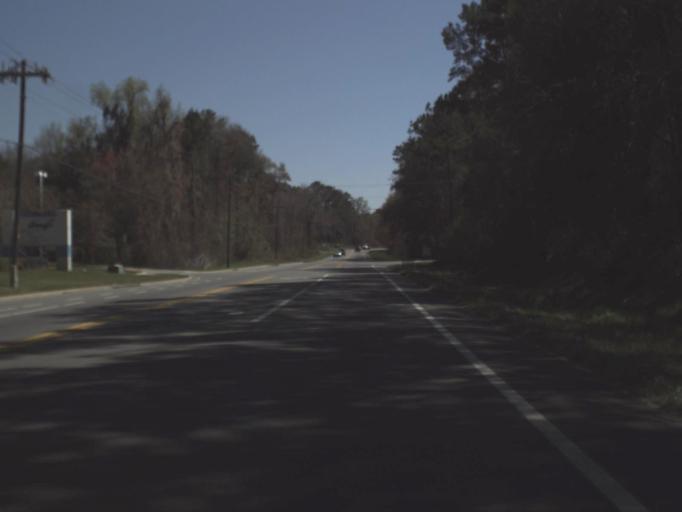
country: US
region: Florida
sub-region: Gadsden County
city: Midway
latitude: 30.5135
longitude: -84.3655
